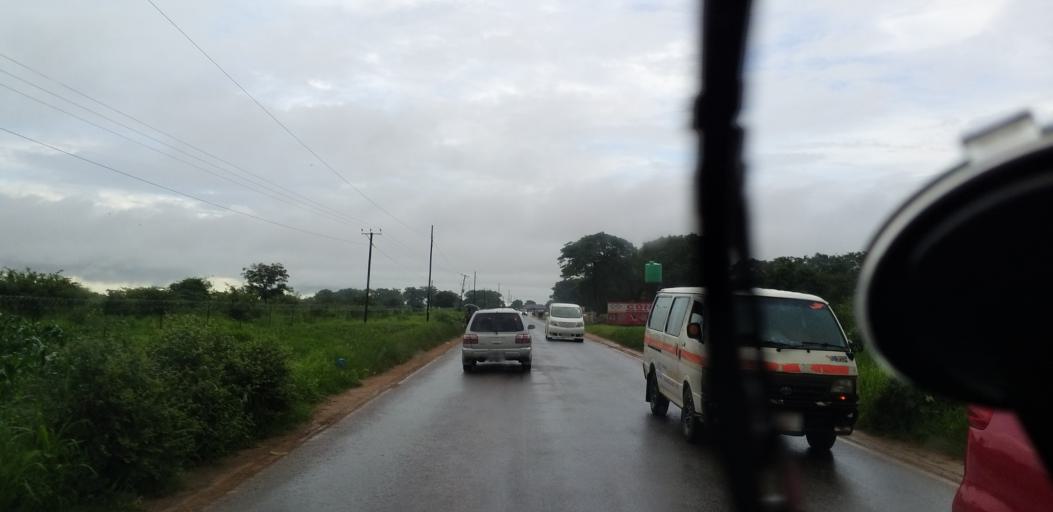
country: ZM
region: Lusaka
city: Lusaka
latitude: -15.5134
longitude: 28.3055
